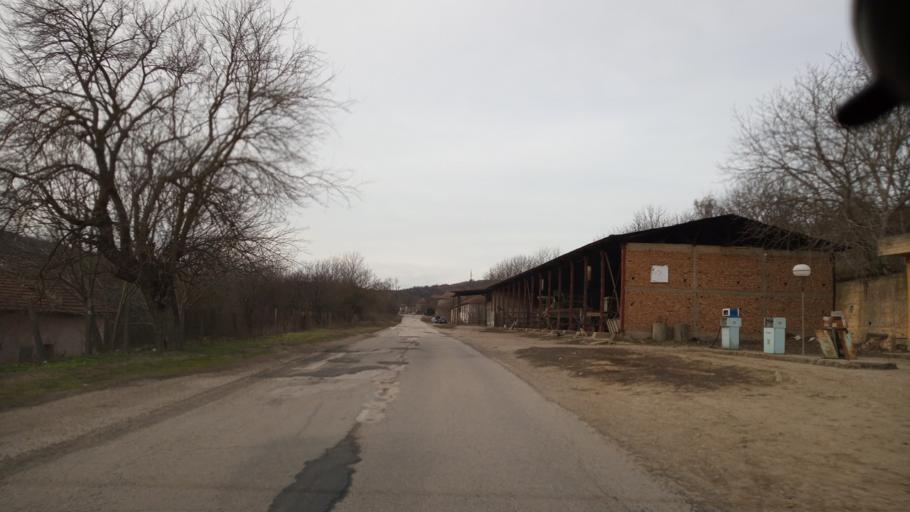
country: BG
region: Pleven
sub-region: Obshtina Belene
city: Belene
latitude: 43.6113
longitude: 25.0155
